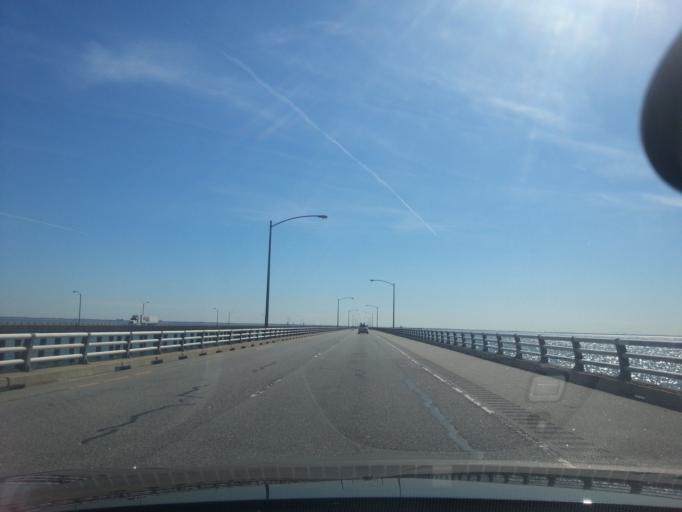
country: US
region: Virginia
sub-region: City of Virginia Beach
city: Virginia Beach
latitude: 37.0191
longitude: -76.0917
